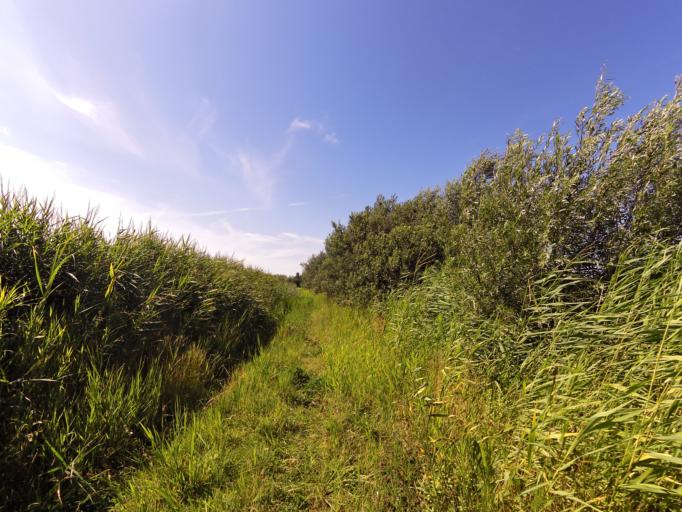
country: NL
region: South Holland
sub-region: Gemeente Goeree-Overflakkee
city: Ouddorp
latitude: 51.7999
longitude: 3.9184
